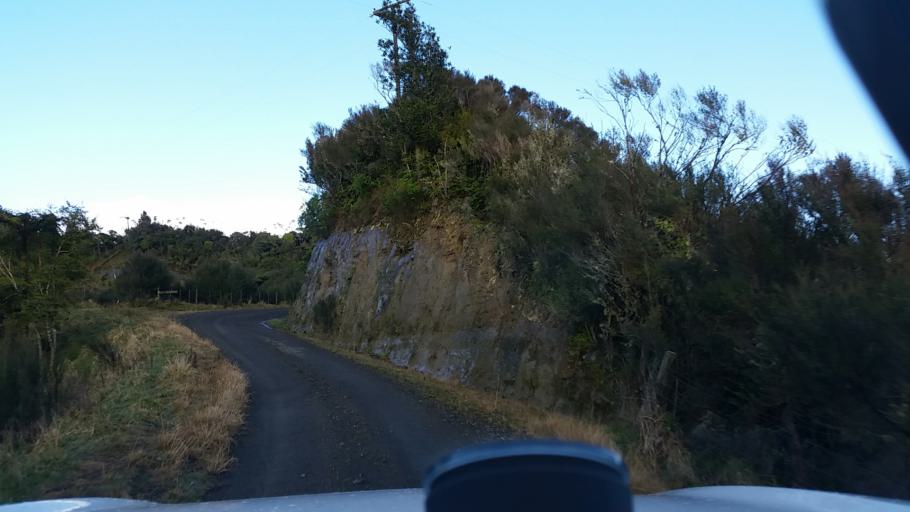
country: NZ
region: Taranaki
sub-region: South Taranaki District
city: Eltham
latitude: -39.4178
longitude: 174.5570
